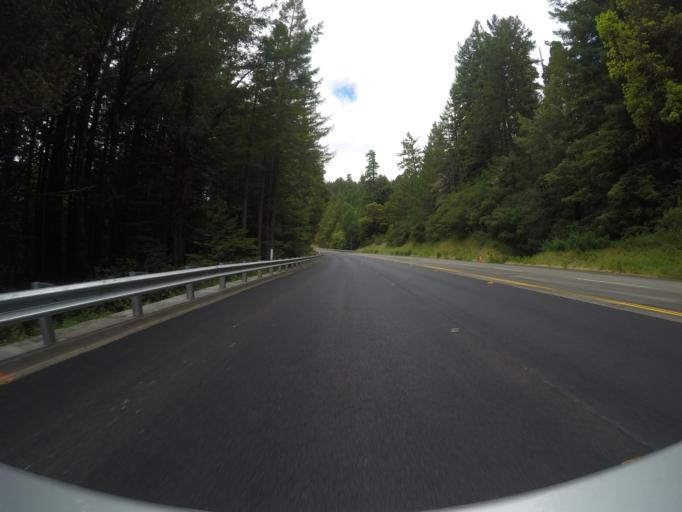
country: US
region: California
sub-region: Humboldt County
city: Redway
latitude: 40.3111
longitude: -123.9079
